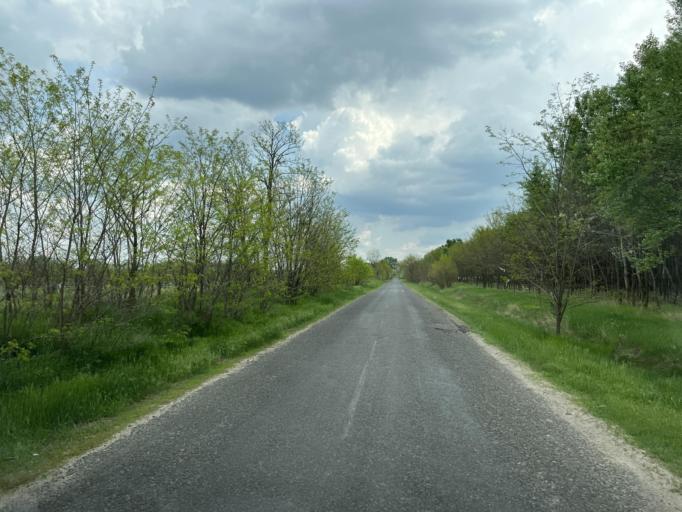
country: HU
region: Pest
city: Nagykoros
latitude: 47.0893
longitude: 19.7724
